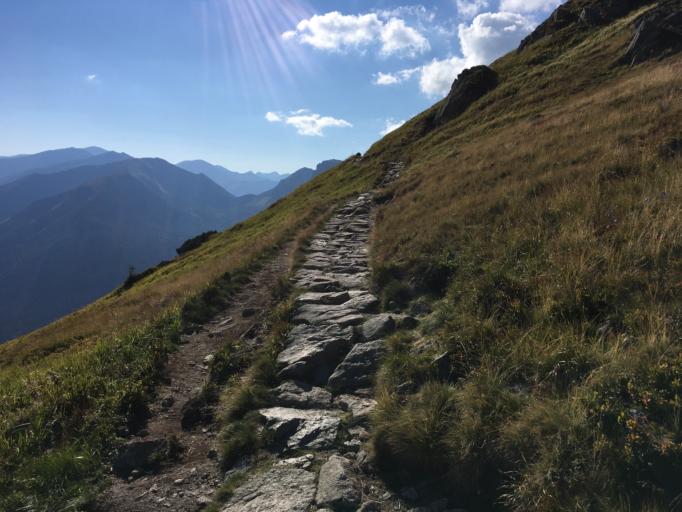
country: PL
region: Lesser Poland Voivodeship
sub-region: Powiat tatrzanski
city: Zakopane
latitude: 49.2304
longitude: 19.9686
